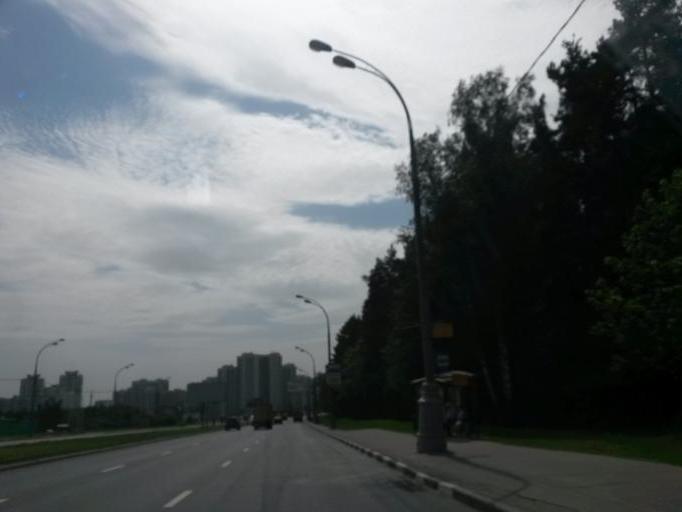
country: RU
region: Moscow
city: Annino
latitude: 55.5579
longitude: 37.5538
